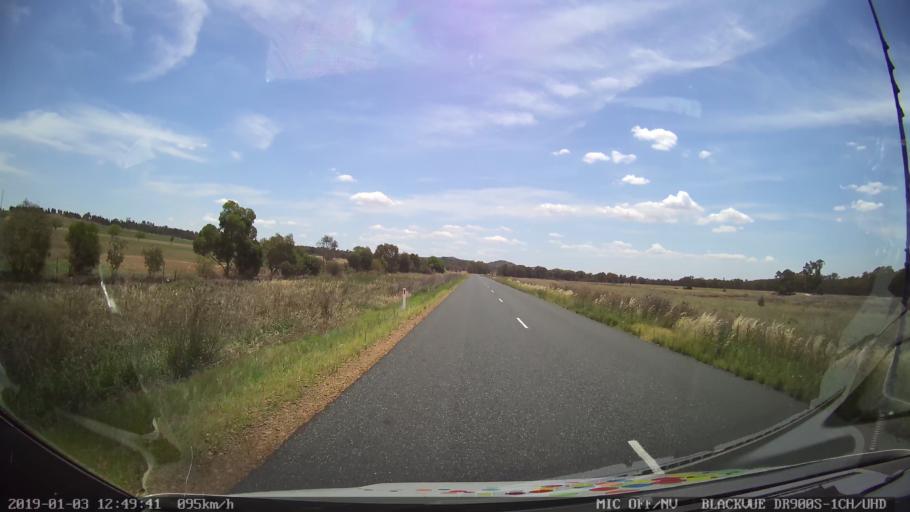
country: AU
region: New South Wales
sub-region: Weddin
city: Grenfell
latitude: -33.7004
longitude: 148.2631
